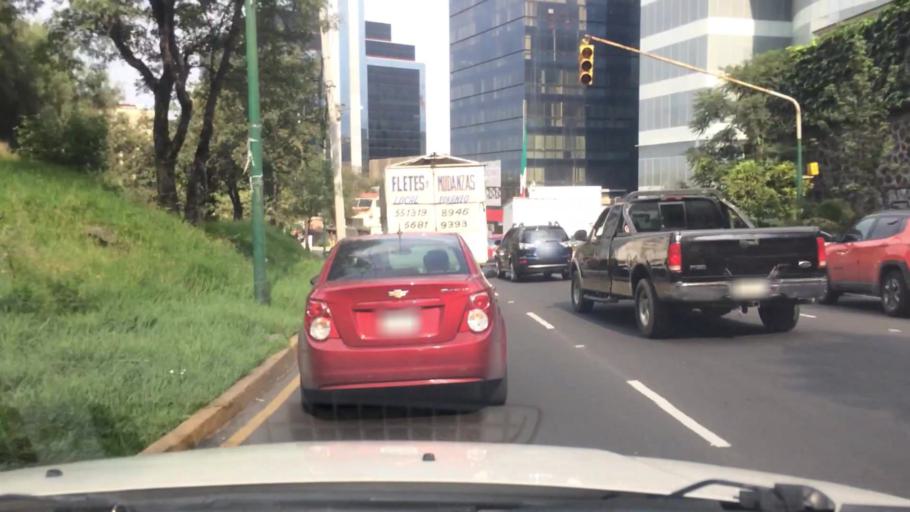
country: MX
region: Mexico City
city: Magdalena Contreras
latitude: 19.2987
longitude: -99.2105
